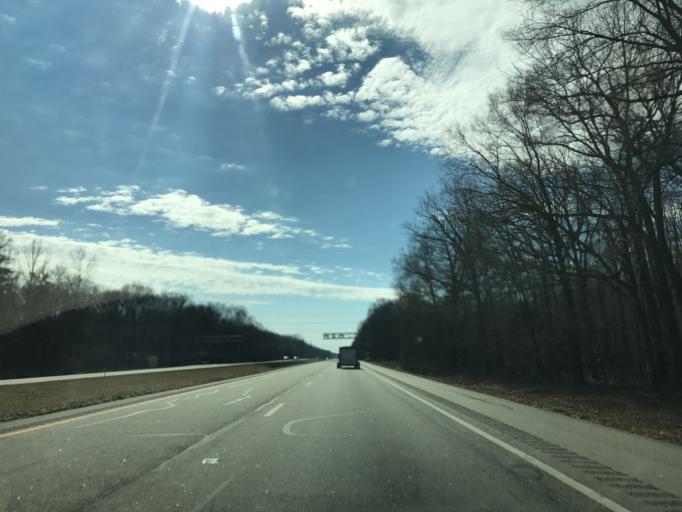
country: US
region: Delaware
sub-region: New Castle County
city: Townsend
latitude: 39.3131
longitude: -75.8485
